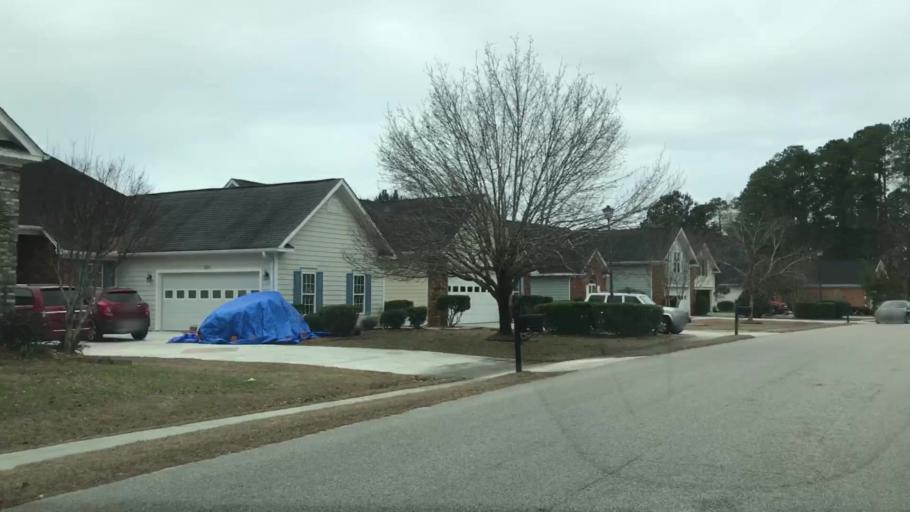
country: US
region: South Carolina
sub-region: Horry County
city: Red Hill
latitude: 33.7716
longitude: -79.0055
